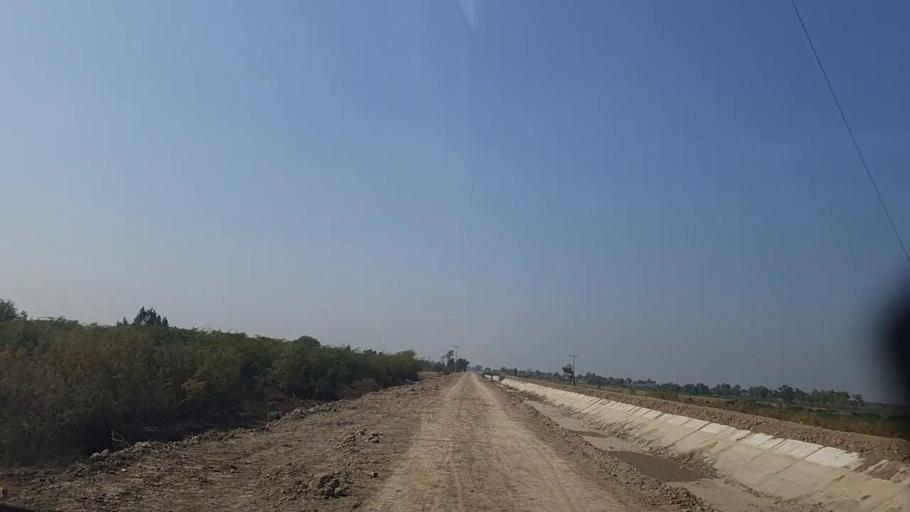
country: PK
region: Sindh
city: Sakrand
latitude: 26.1467
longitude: 68.3488
